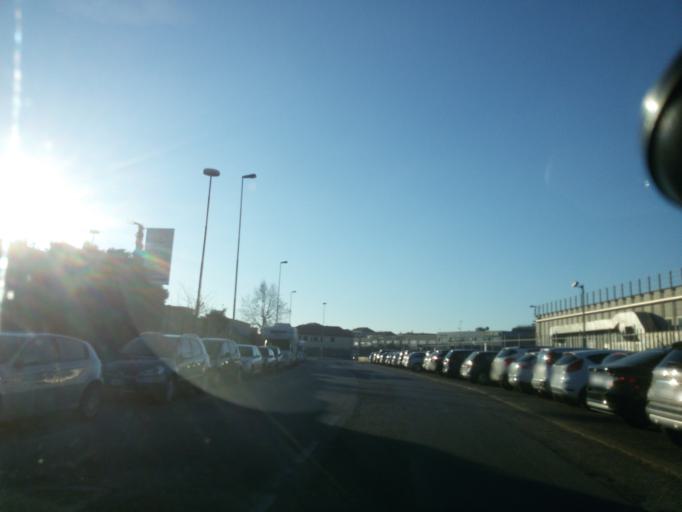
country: IT
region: Liguria
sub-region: Provincia di Savona
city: Savona
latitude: 44.3006
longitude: 8.4553
